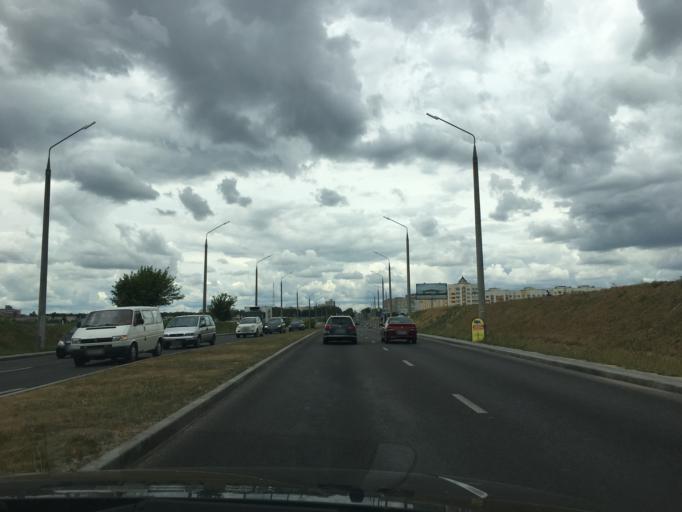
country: BY
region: Grodnenskaya
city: Hrodna
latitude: 53.6354
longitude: 23.8502
